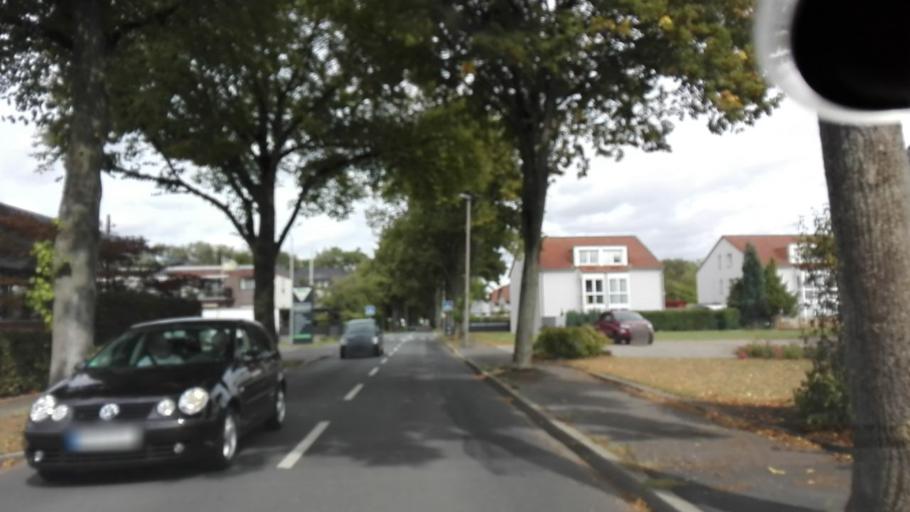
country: DE
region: North Rhine-Westphalia
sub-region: Regierungsbezirk Arnsberg
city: Unna
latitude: 51.5219
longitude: 7.6785
